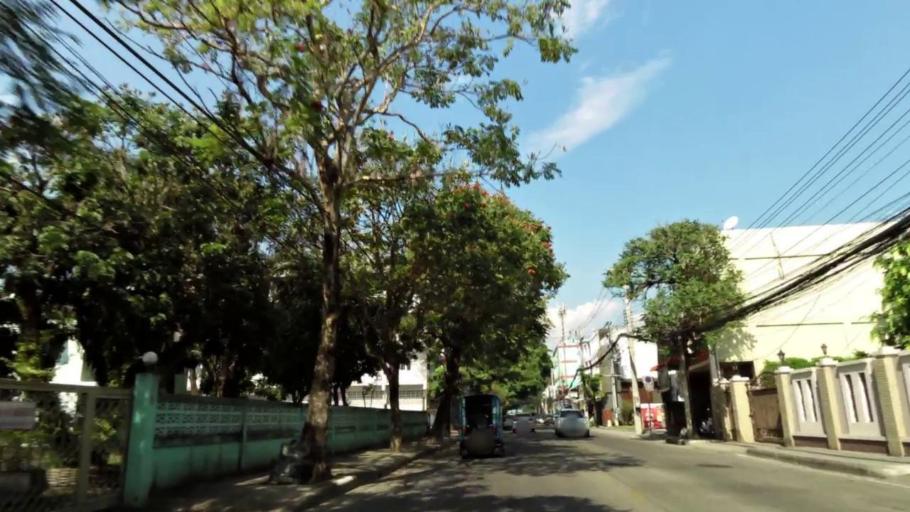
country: TH
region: Chiang Rai
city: Chiang Rai
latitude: 19.9099
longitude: 99.8329
